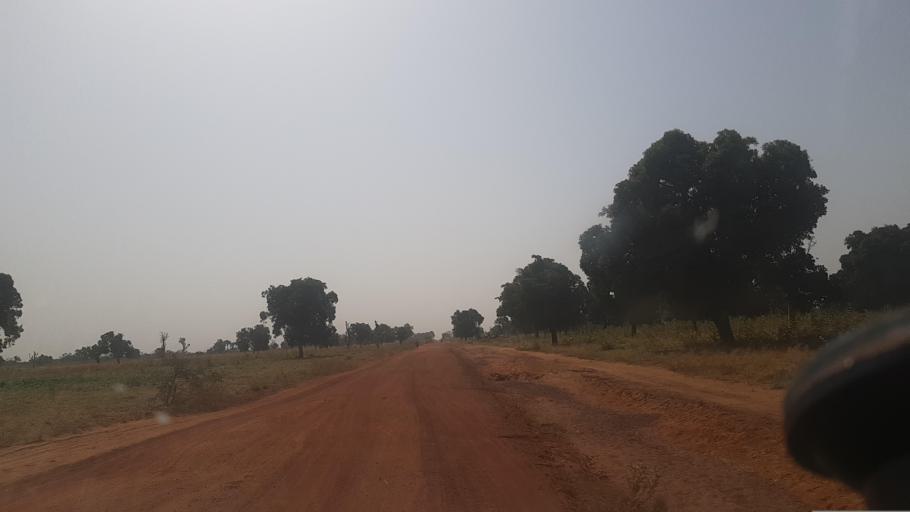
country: ML
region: Segou
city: Baroueli
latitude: 13.0034
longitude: -6.4195
